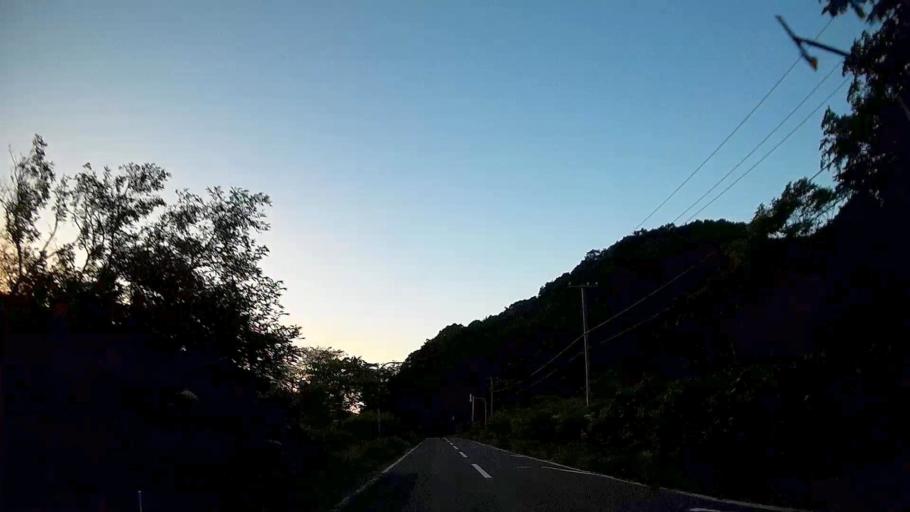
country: JP
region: Hokkaido
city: Iwanai
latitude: 42.6784
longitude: 140.0701
